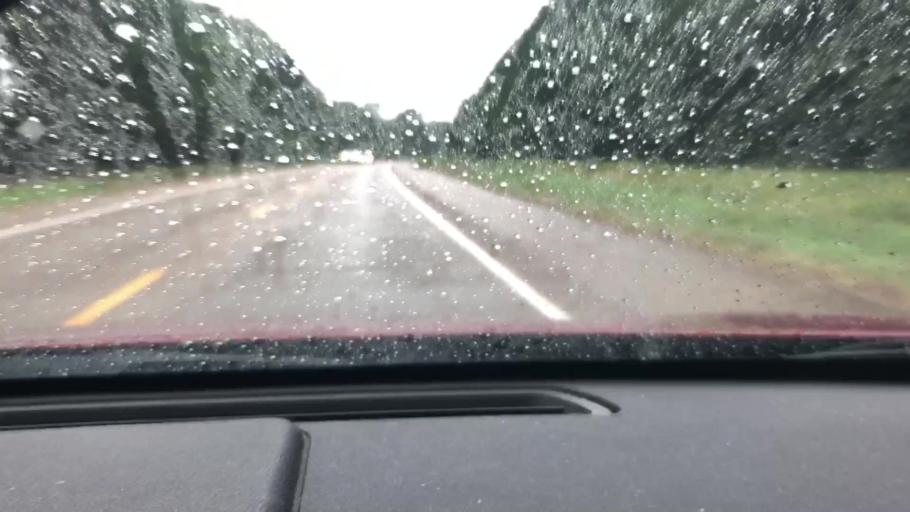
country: US
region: Arkansas
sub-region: Columbia County
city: Magnolia
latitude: 33.2973
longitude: -93.2599
